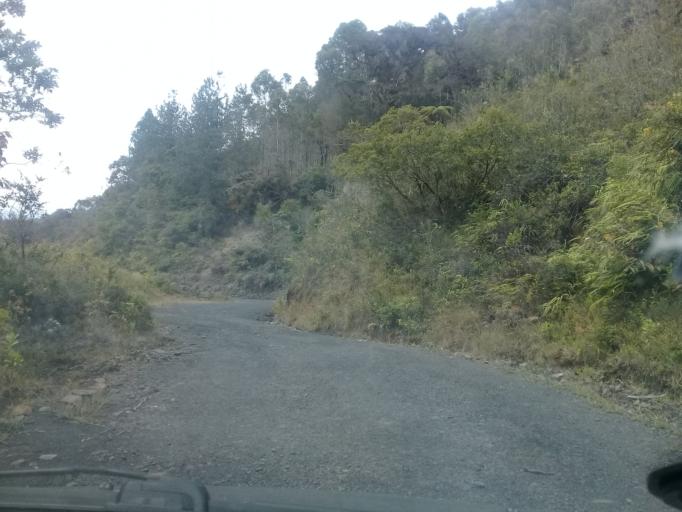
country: CO
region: Cundinamarca
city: Gachala
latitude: 4.7030
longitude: -73.4475
